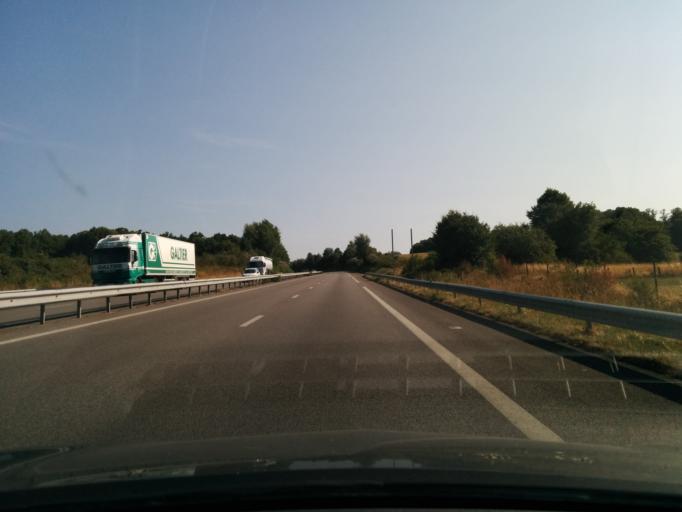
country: FR
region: Limousin
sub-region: Departement de la Haute-Vienne
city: Saint-Germain-les-Belles
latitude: 45.6081
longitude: 1.4479
